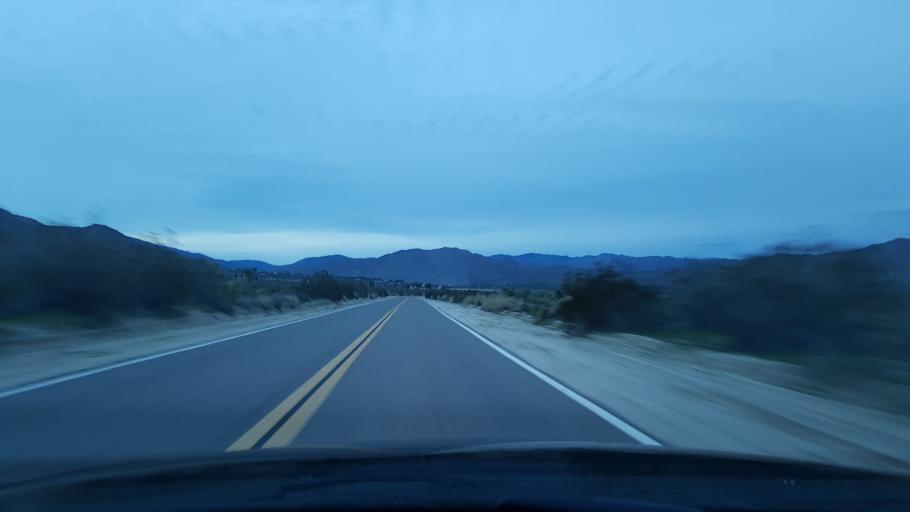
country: US
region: California
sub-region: San Diego County
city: Julian
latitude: 33.0459
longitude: -116.4133
